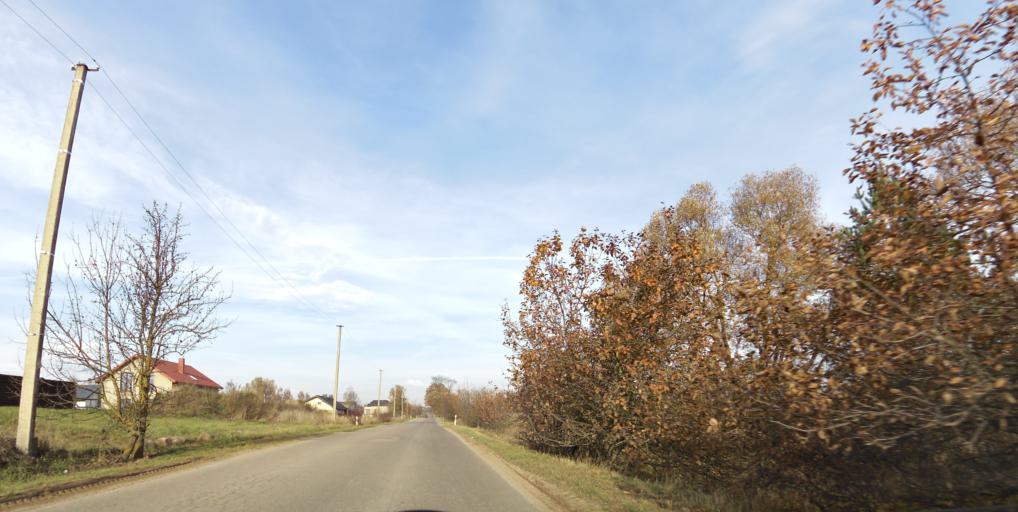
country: LT
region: Vilnius County
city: Pilaite
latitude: 54.7171
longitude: 25.1591
